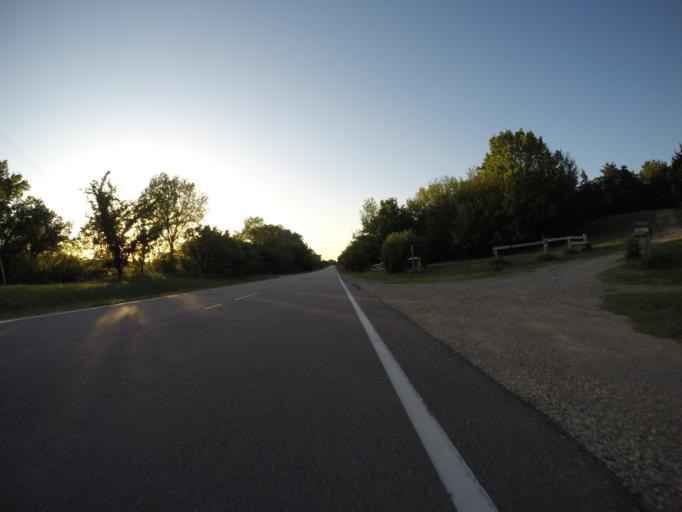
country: US
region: Kansas
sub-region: Riley County
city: Fort Riley North
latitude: 39.2403
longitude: -96.7628
